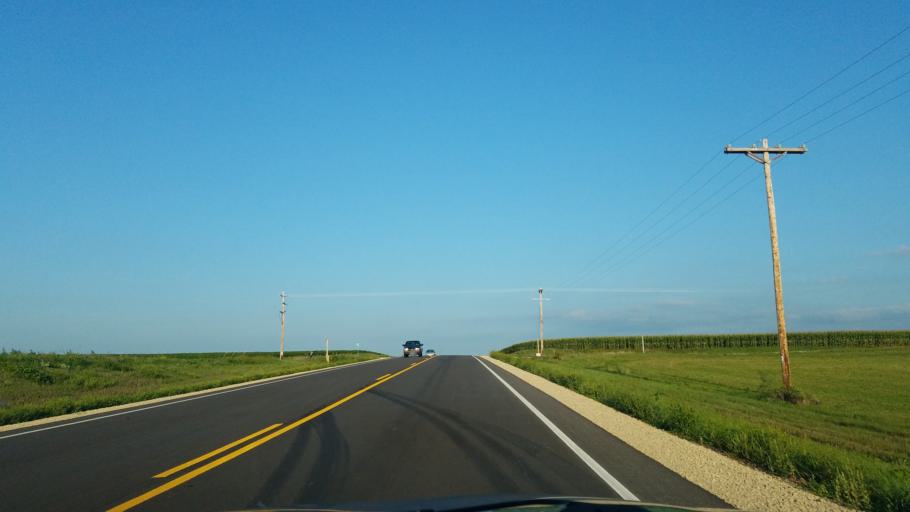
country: US
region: Wisconsin
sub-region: Saint Croix County
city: Hammond
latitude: 45.0791
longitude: -92.4173
